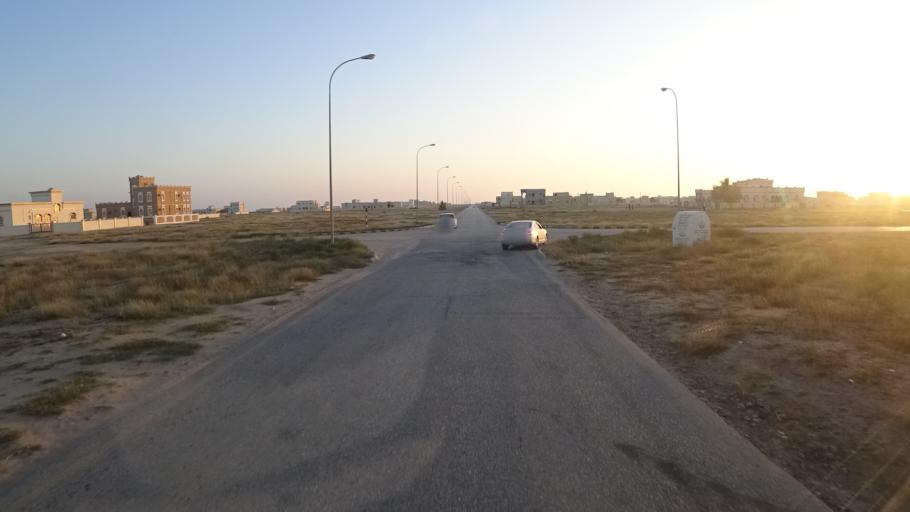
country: OM
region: Zufar
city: Salalah
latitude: 16.9900
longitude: 54.7167
